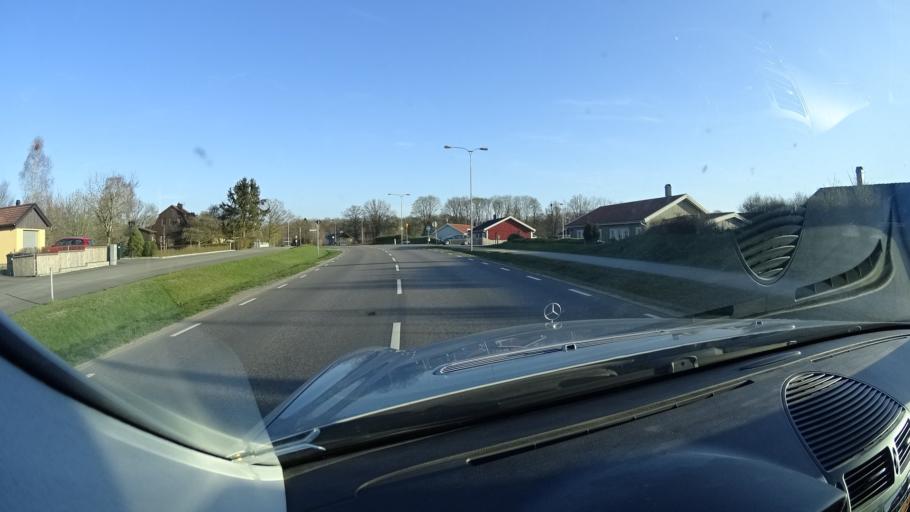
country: SE
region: Skane
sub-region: Hoors Kommun
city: Satofta
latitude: 55.9162
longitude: 13.5462
